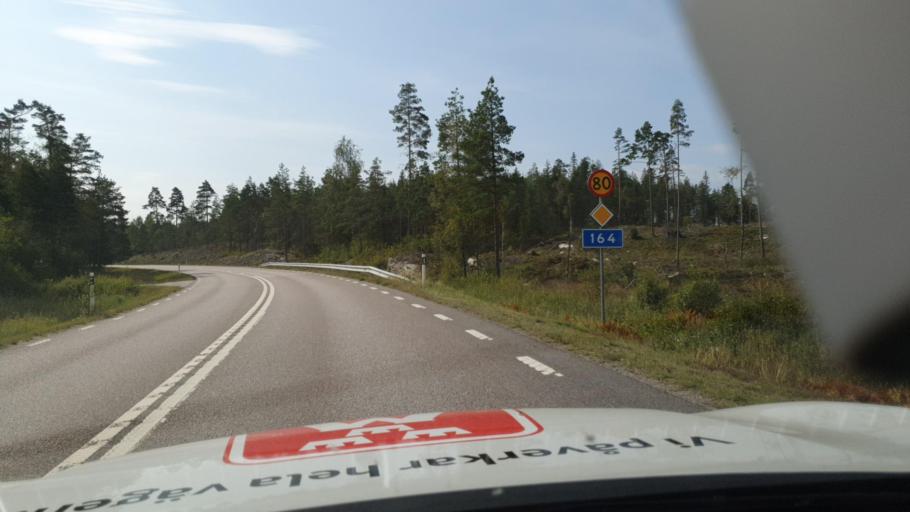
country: SE
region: Vaestra Goetaland
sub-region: Dals-Ed Kommun
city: Ed
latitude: 58.8723
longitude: 11.7707
